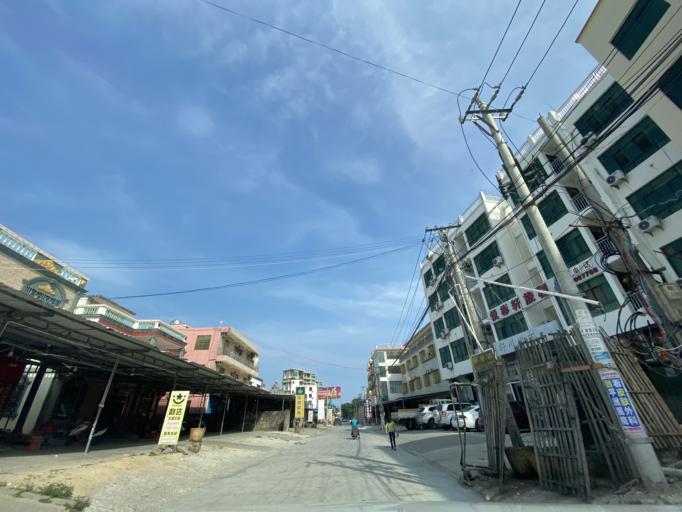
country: CN
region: Hainan
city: Yingzhou
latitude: 18.4037
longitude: 109.8430
